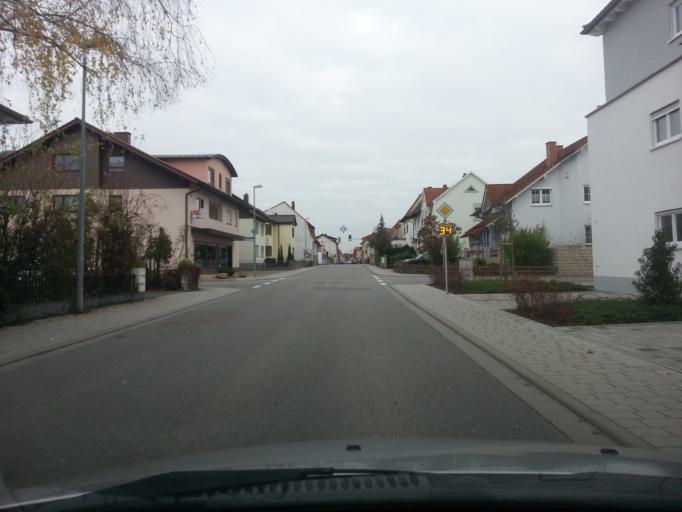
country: DE
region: Baden-Wuerttemberg
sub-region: Karlsruhe Region
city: Reilingen
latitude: 49.2891
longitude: 8.5637
